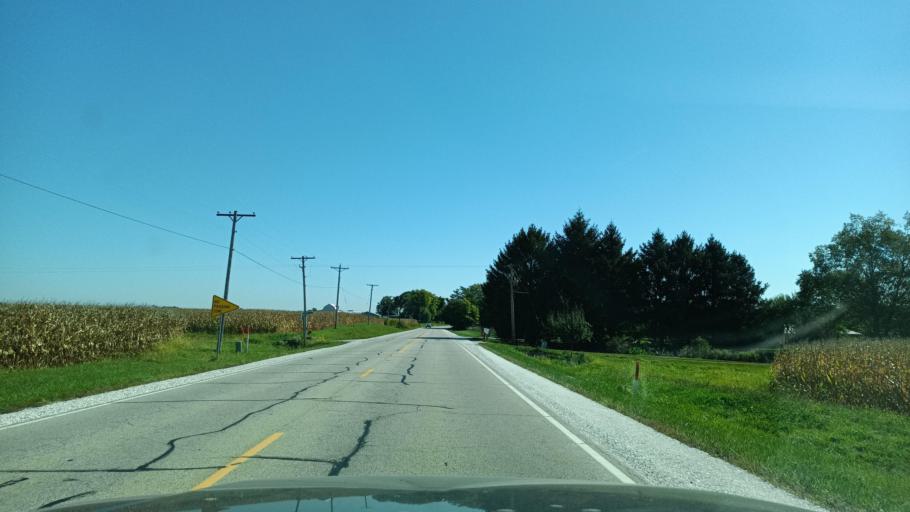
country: US
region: Illinois
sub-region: Peoria County
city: Hanna City
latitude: 40.7945
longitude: -89.7812
